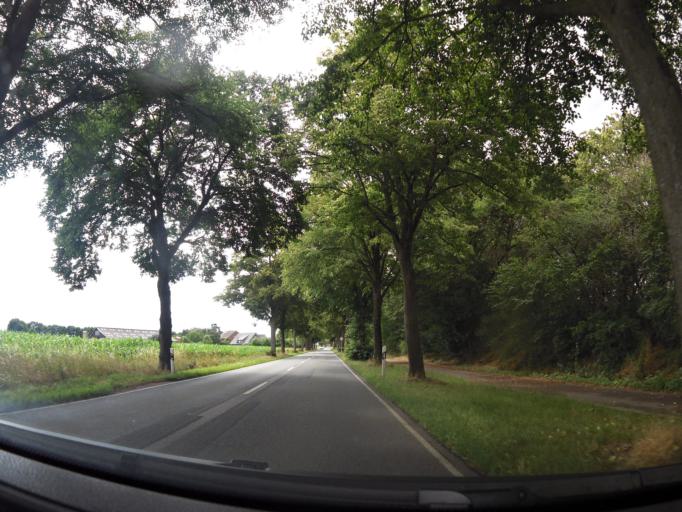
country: DE
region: North Rhine-Westphalia
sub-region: Regierungsbezirk Dusseldorf
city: Xanten
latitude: 51.6107
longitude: 6.4602
